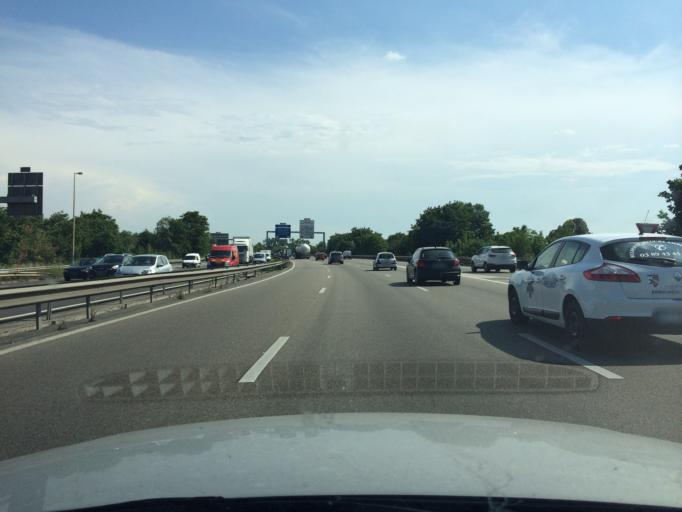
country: FR
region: Alsace
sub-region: Departement du Bas-Rhin
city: Strasbourg
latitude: 48.5822
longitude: 7.7236
